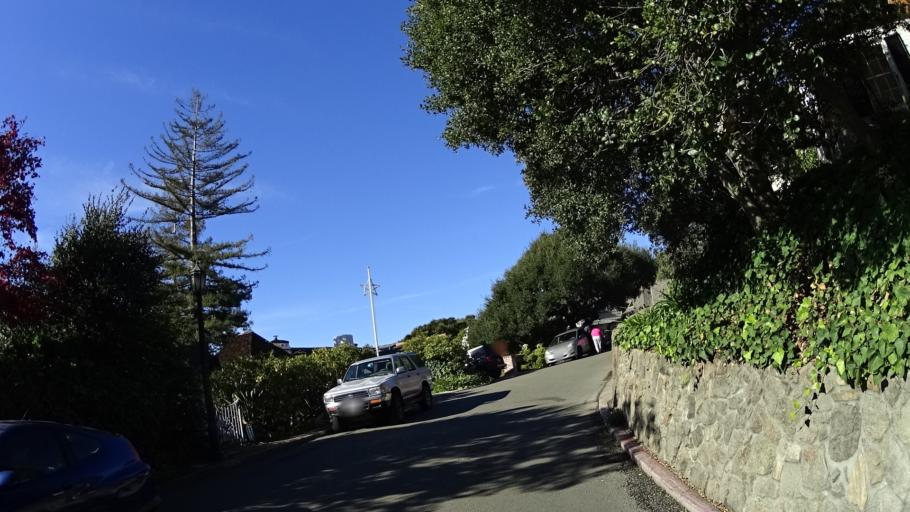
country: US
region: California
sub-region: Alameda County
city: Piedmont
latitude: 37.8177
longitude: -122.2313
